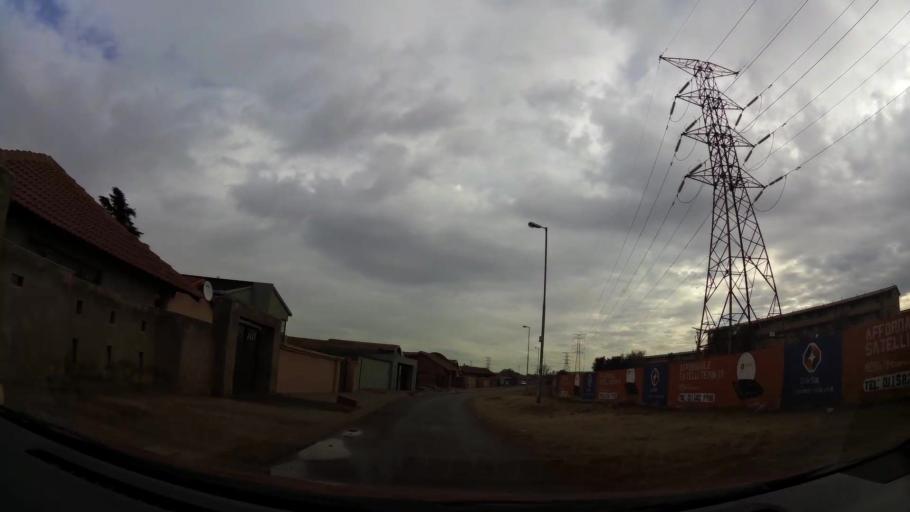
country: ZA
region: Gauteng
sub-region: City of Johannesburg Metropolitan Municipality
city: Soweto
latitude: -26.2793
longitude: 27.8438
